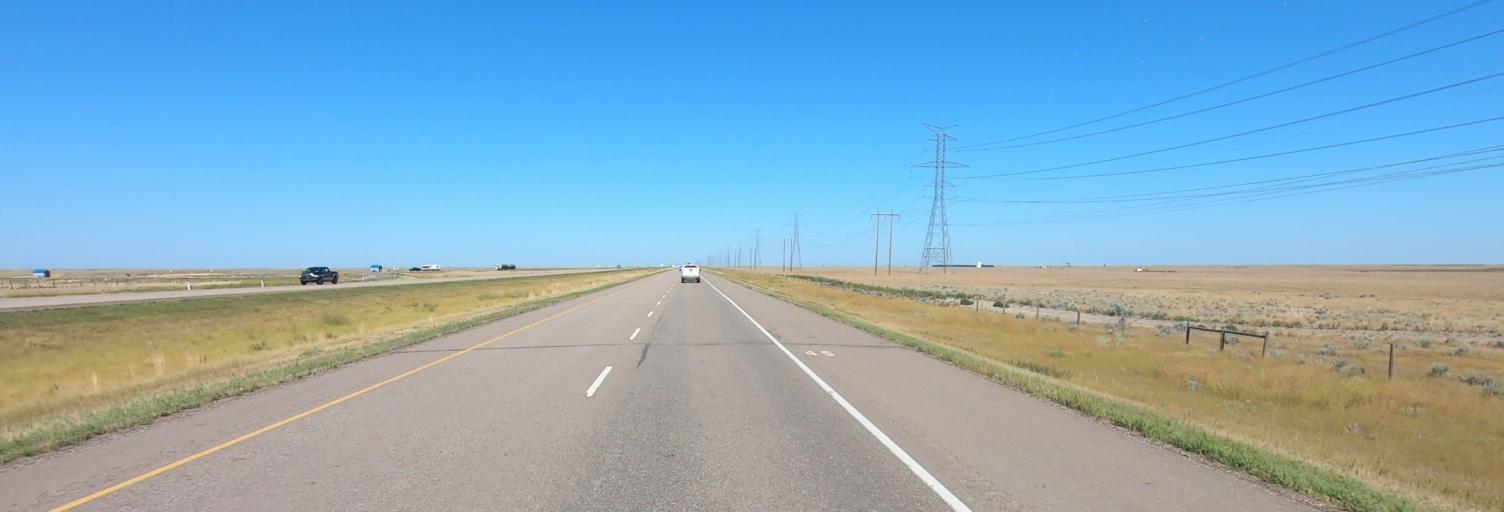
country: CA
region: Alberta
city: Brooks
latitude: 50.3979
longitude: -111.4831
